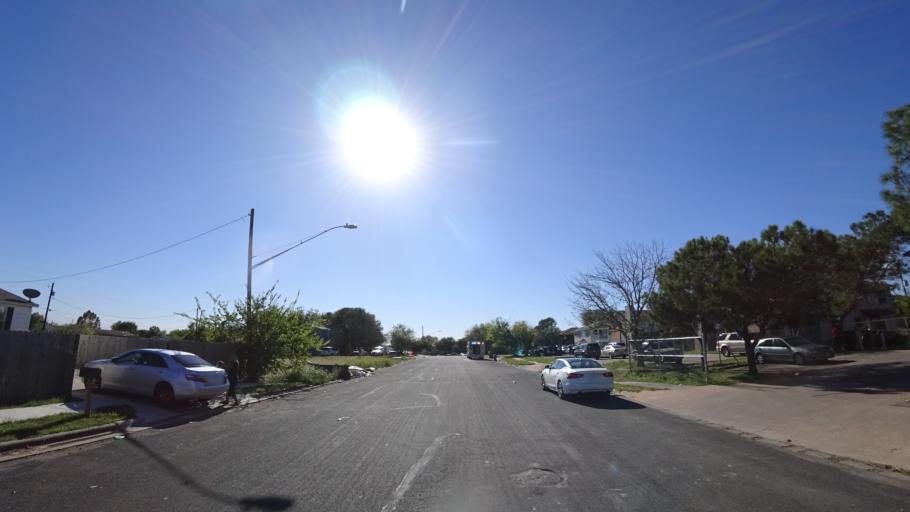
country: US
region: Texas
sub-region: Travis County
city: Hornsby Bend
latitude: 30.2944
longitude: -97.6287
